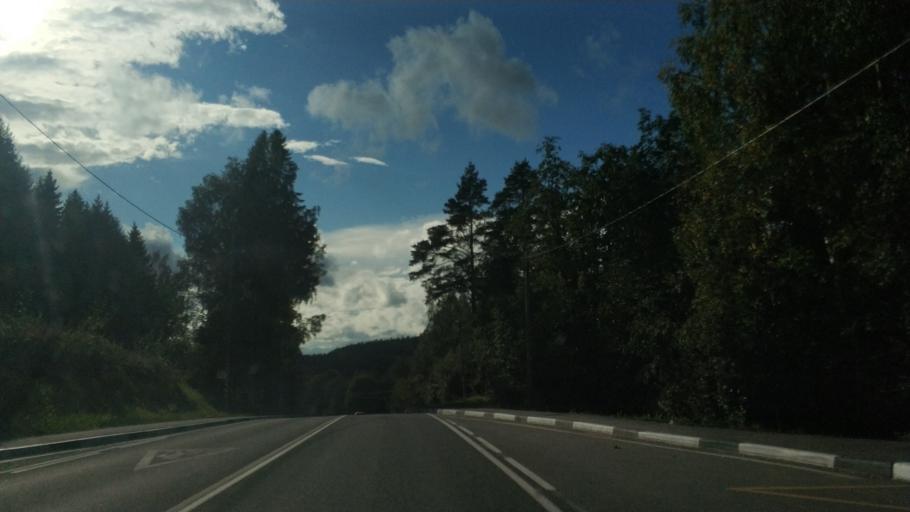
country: RU
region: Republic of Karelia
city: Lakhdenpokh'ya
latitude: 61.5233
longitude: 30.1669
